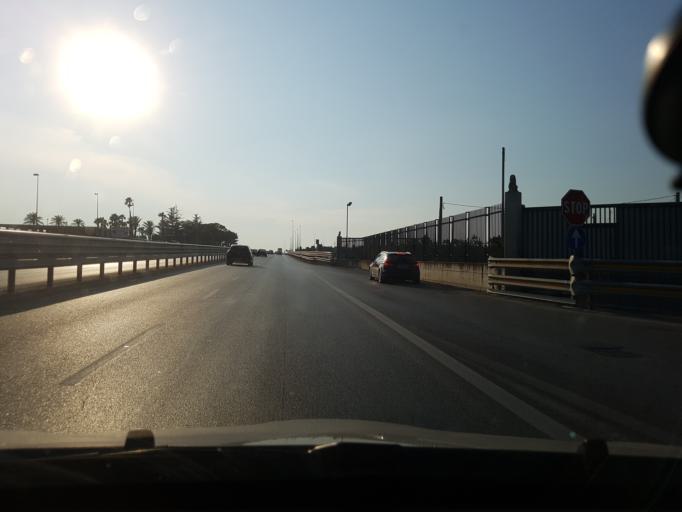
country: IT
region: Apulia
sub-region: Provincia di Foggia
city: Cerignola
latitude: 41.2780
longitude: 15.8625
